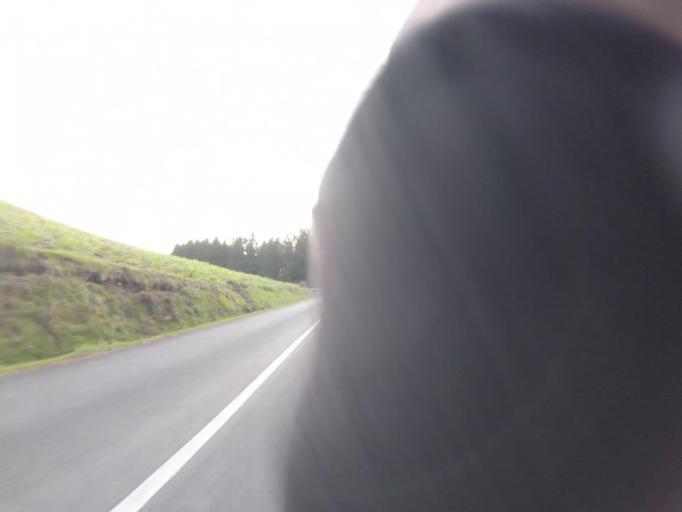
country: ES
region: Navarre
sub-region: Provincia de Navarra
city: Arano
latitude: 43.2441
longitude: -1.8365
